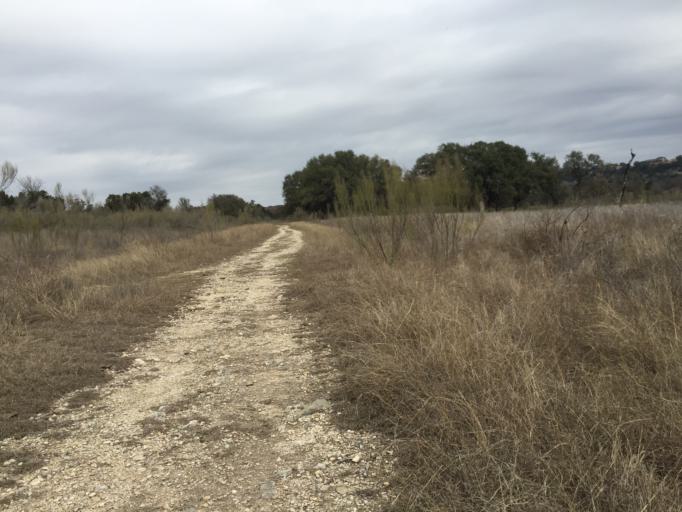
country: US
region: Texas
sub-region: Bell County
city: Nolanville
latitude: 31.0273
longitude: -97.6175
